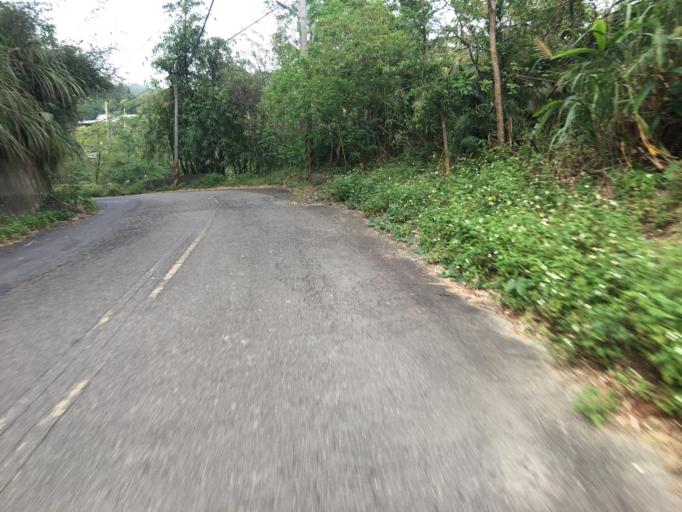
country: TW
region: Taiwan
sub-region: Hsinchu
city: Hsinchu
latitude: 24.7124
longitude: 121.0591
